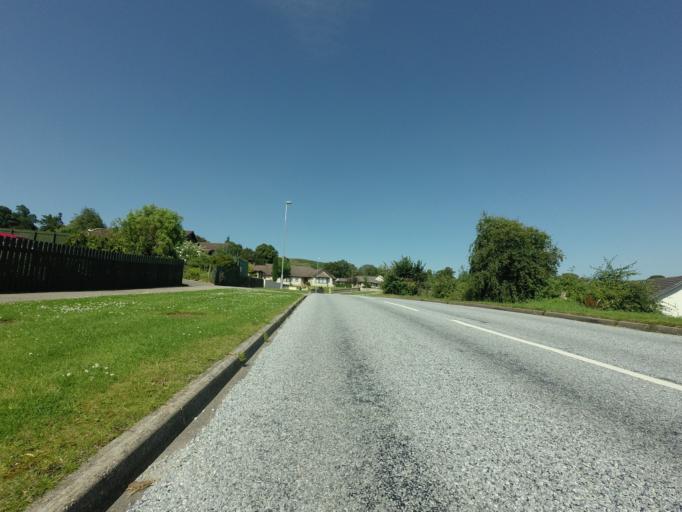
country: GB
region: Scotland
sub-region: Highland
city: Dingwall
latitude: 57.6094
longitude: -4.4199
